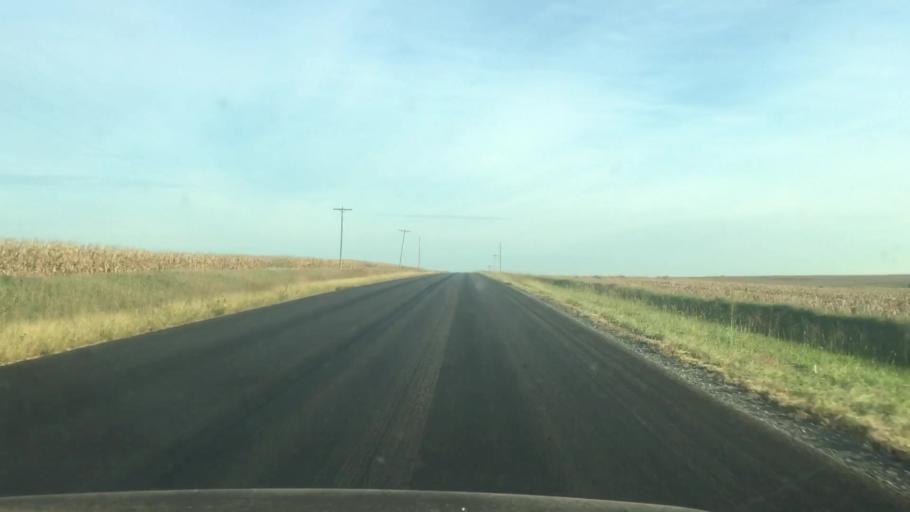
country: US
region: Kansas
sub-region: Marshall County
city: Marysville
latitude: 39.9042
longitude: -96.6011
